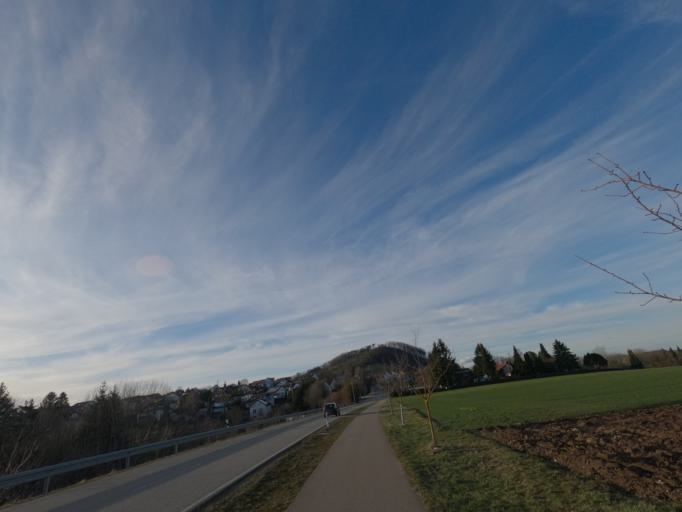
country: DE
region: Baden-Wuerttemberg
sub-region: Regierungsbezirk Stuttgart
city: Waldstetten
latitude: 48.7476
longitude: 9.7990
